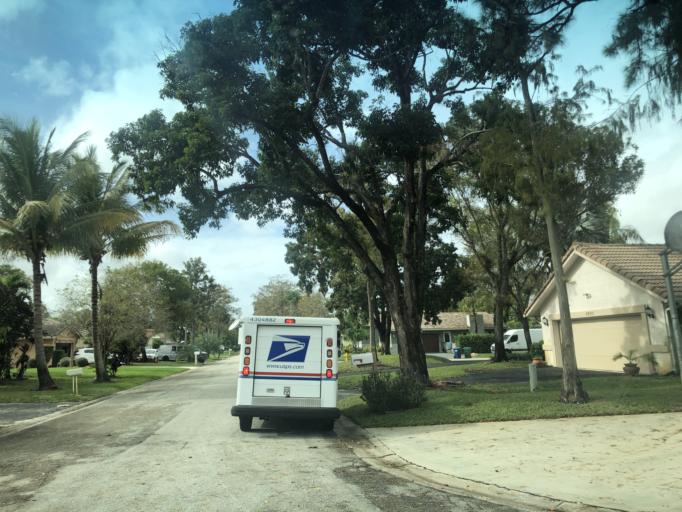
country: US
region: Florida
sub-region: Broward County
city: Margate
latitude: 26.2490
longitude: -80.2357
